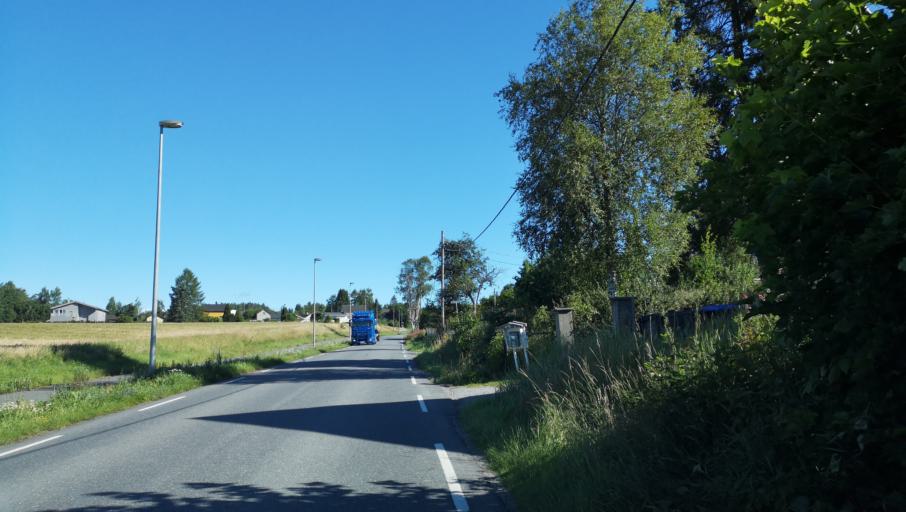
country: NO
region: Ostfold
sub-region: Hobol
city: Knappstad
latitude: 59.6214
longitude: 11.0236
